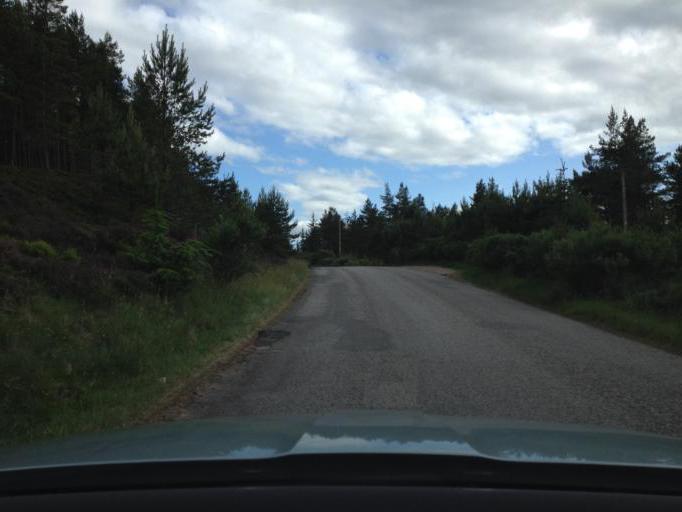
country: GB
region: Scotland
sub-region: Aberdeenshire
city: Banchory
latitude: 56.9898
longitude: -2.5766
